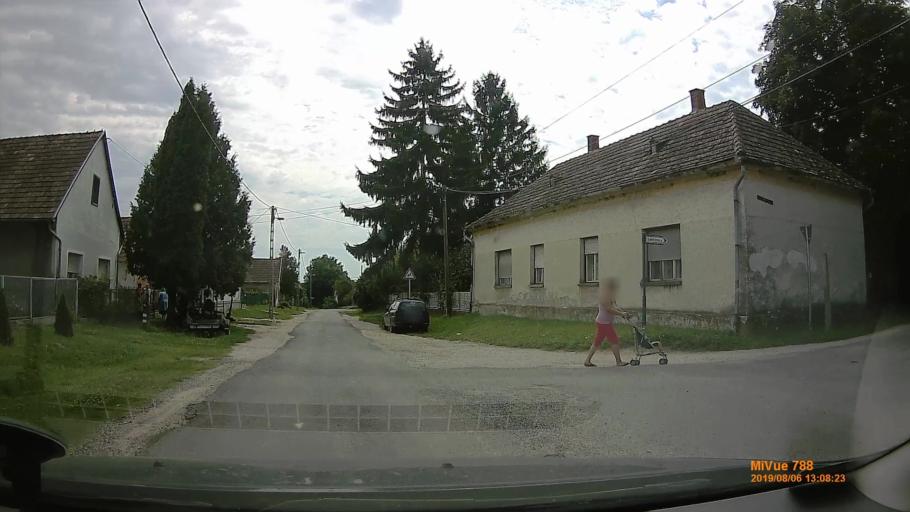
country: HU
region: Zala
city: Pacsa
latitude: 46.6270
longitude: 17.0621
